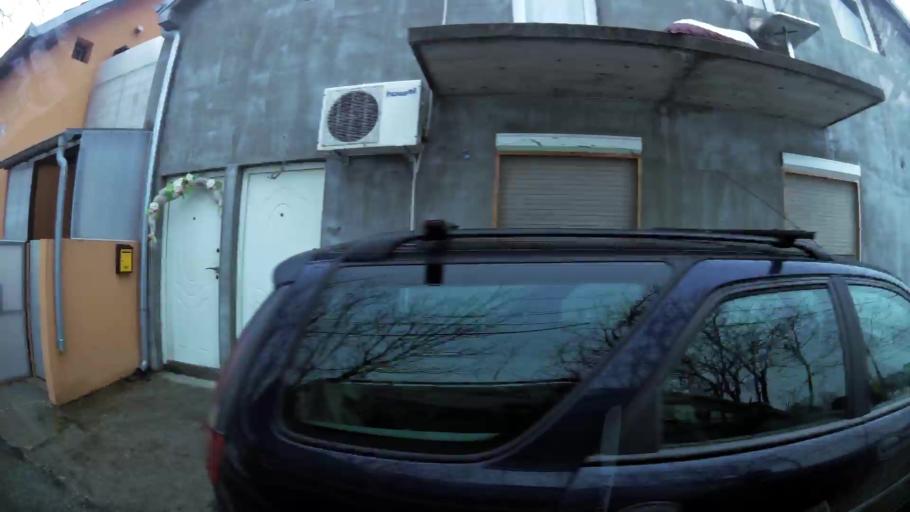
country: RS
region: Central Serbia
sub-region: Belgrade
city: Zemun
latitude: 44.8470
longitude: 20.3901
